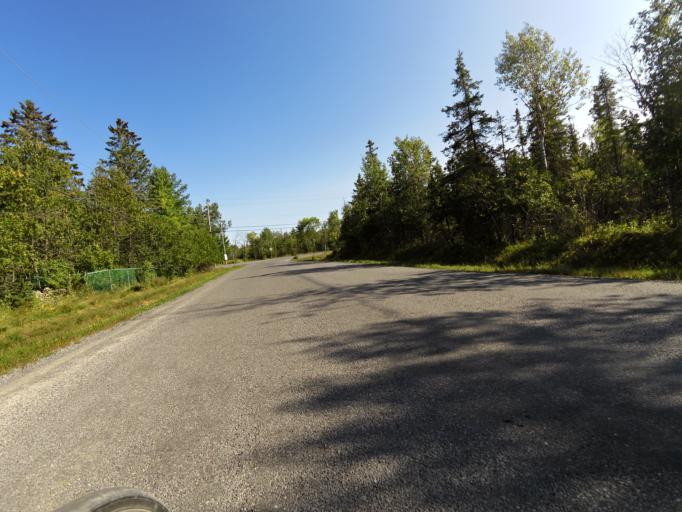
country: CA
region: Ontario
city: Bells Corners
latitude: 45.4749
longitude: -75.9970
